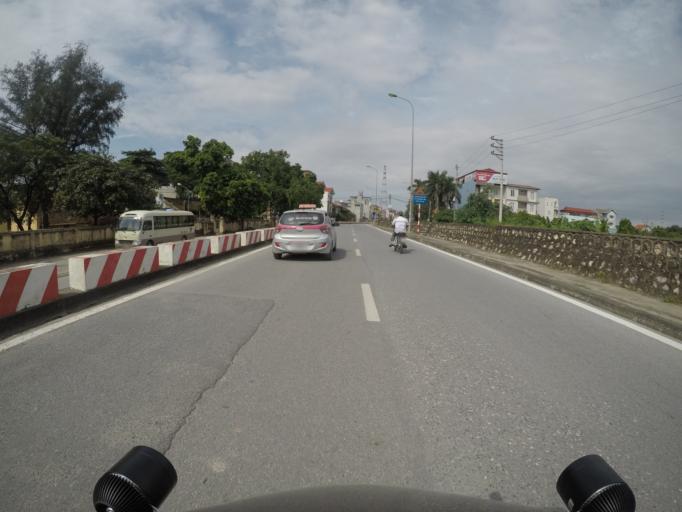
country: VN
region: Ha Noi
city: Tay Ho
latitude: 21.0919
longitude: 105.7835
